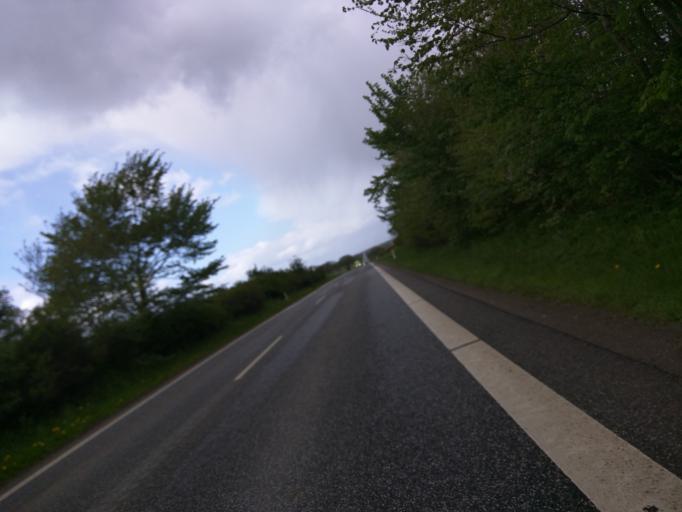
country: DK
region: Central Jutland
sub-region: Silkeborg Kommune
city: Kjellerup
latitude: 56.3559
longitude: 9.4356
